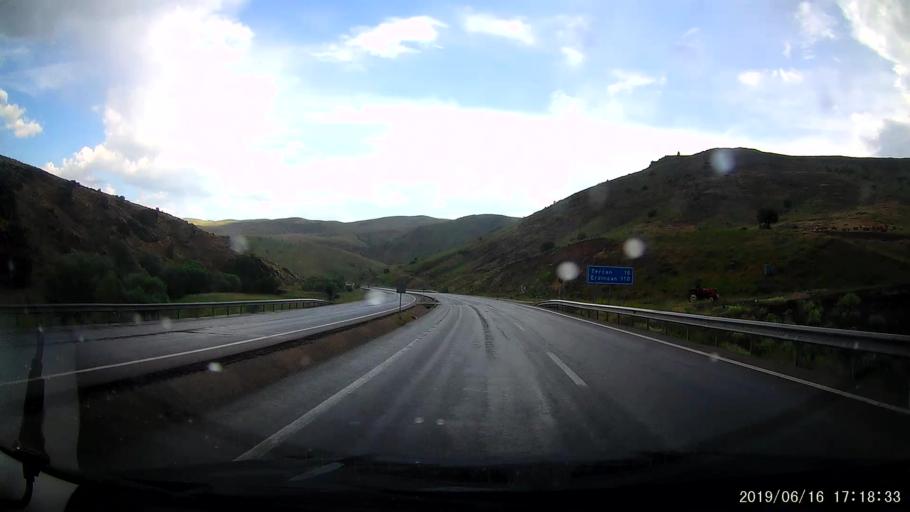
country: TR
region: Erzincan
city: Tercan
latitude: 39.8125
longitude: 40.5287
